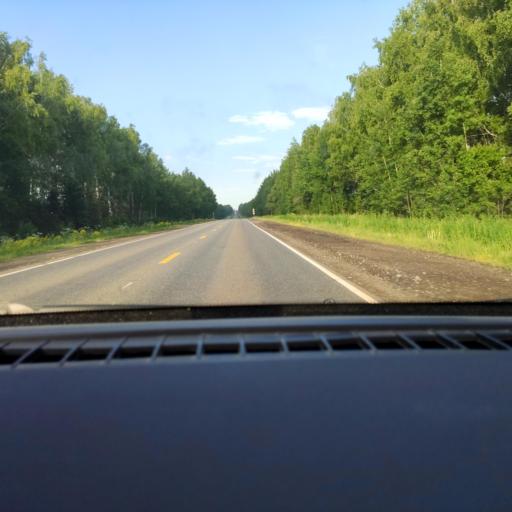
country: RU
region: Udmurtiya
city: Votkinsk
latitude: 56.9863
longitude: 53.7900
